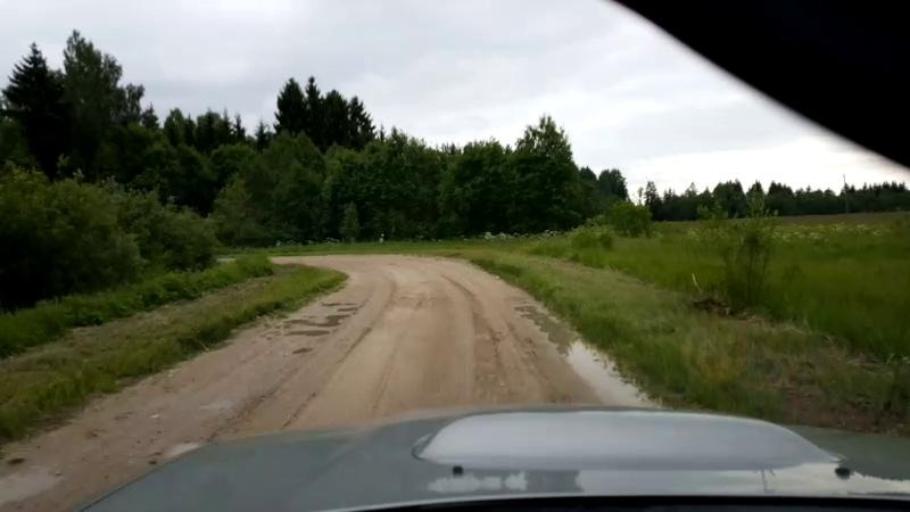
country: EE
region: Paernumaa
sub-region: Halinga vald
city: Parnu-Jaagupi
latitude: 58.5490
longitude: 24.5767
